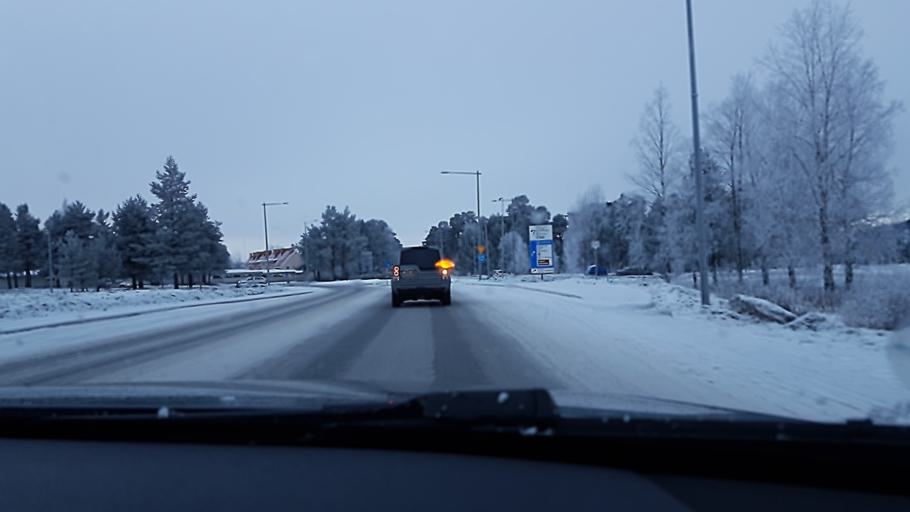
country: SE
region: Jaemtland
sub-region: OEstersunds Kommun
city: Ostersund
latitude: 63.1891
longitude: 14.6532
